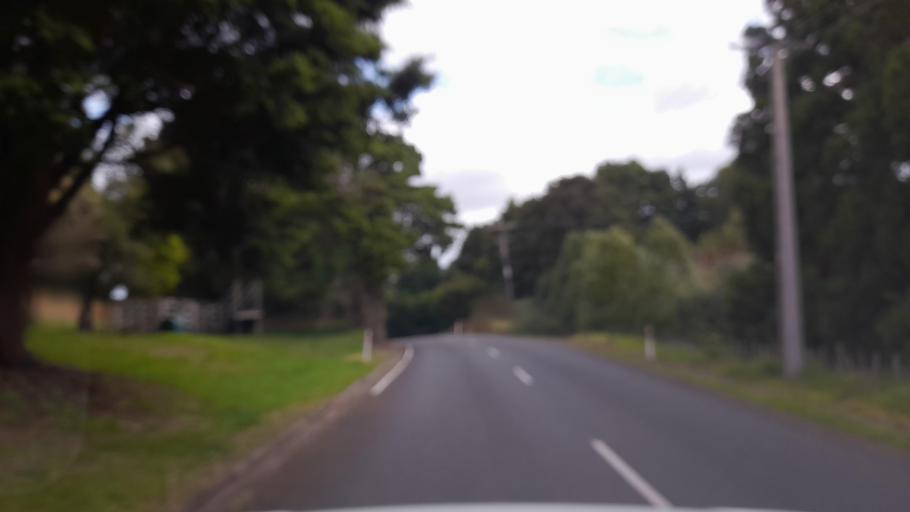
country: NZ
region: Northland
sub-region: Whangarei
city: Maungatapere
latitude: -35.7582
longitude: 174.2360
